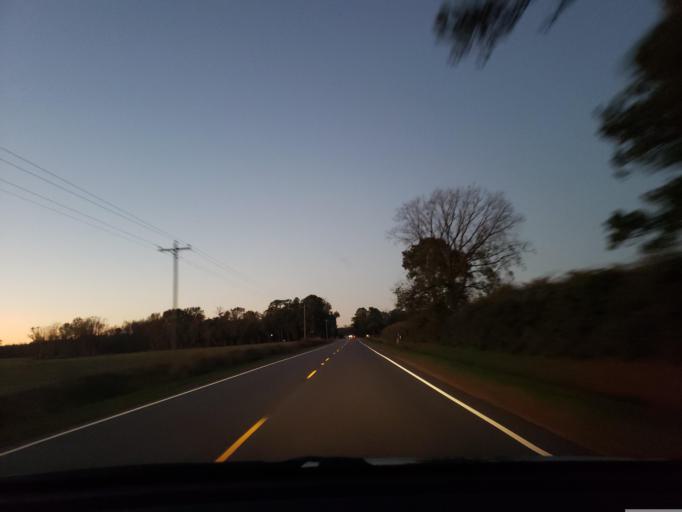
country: US
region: North Carolina
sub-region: Duplin County
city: Kenansville
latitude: 34.9328
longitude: -77.9407
